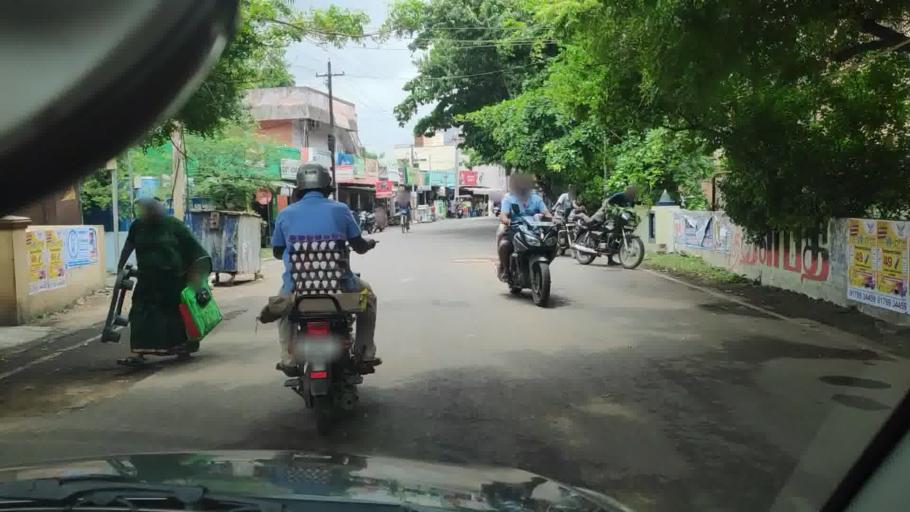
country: IN
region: Tamil Nadu
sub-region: Thiruvallur
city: Ambattur
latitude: 13.1195
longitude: 80.1578
